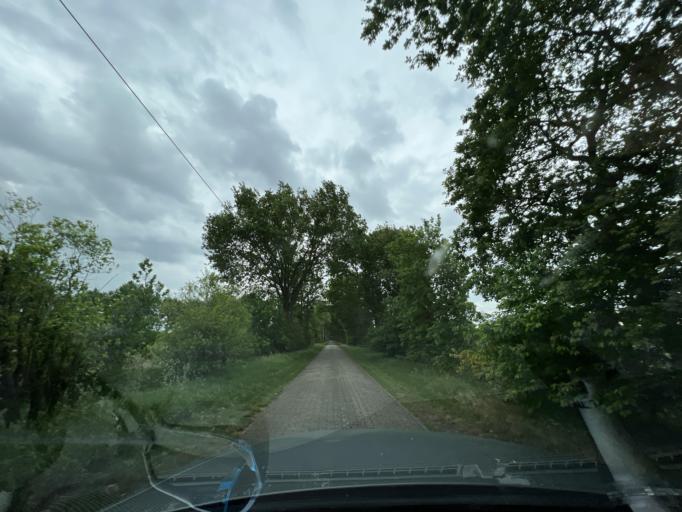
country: DE
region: Lower Saxony
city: Hatten
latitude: 53.0408
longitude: 8.3154
